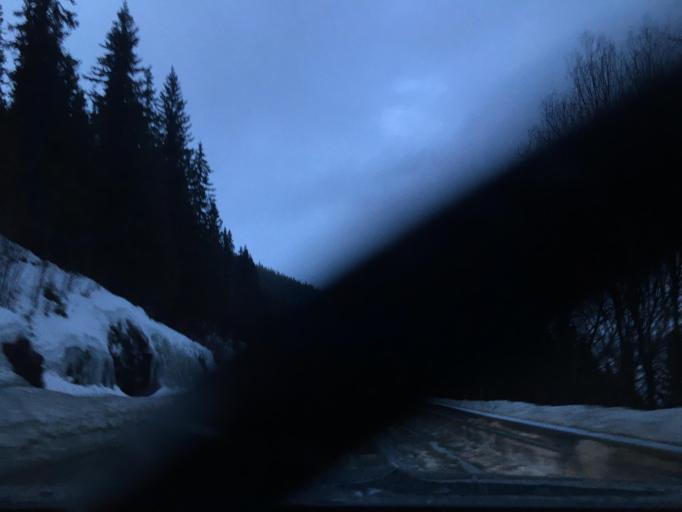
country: NO
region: Nordland
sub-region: Rana
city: Hauknes
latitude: 66.2841
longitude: 13.9064
